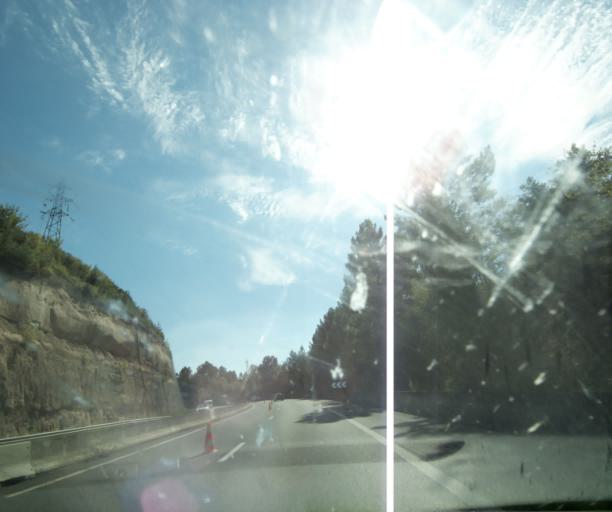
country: FR
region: Limousin
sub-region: Departement de la Correze
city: Brive-la-Gaillarde
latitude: 45.1145
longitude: 1.4998
